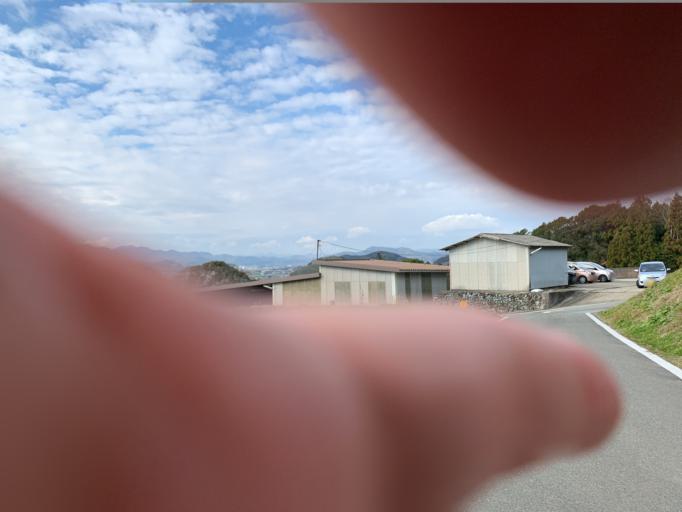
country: JP
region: Kyoto
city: Kameoka
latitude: 35.0578
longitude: 135.5798
